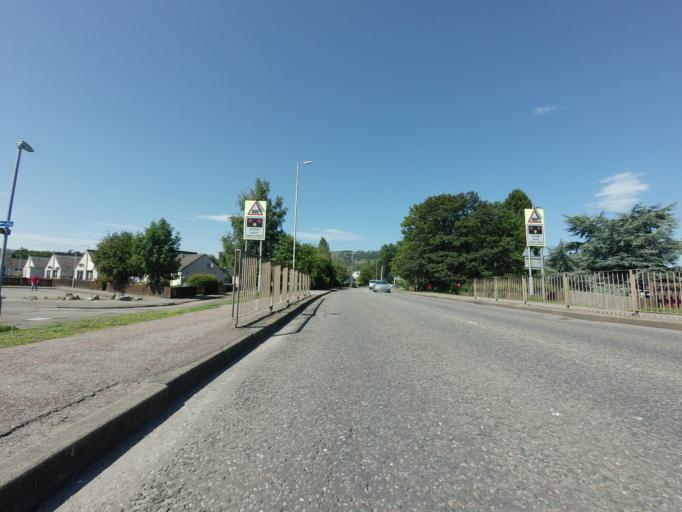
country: GB
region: Scotland
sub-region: Highland
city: Dingwall
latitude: 57.5983
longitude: -4.4325
